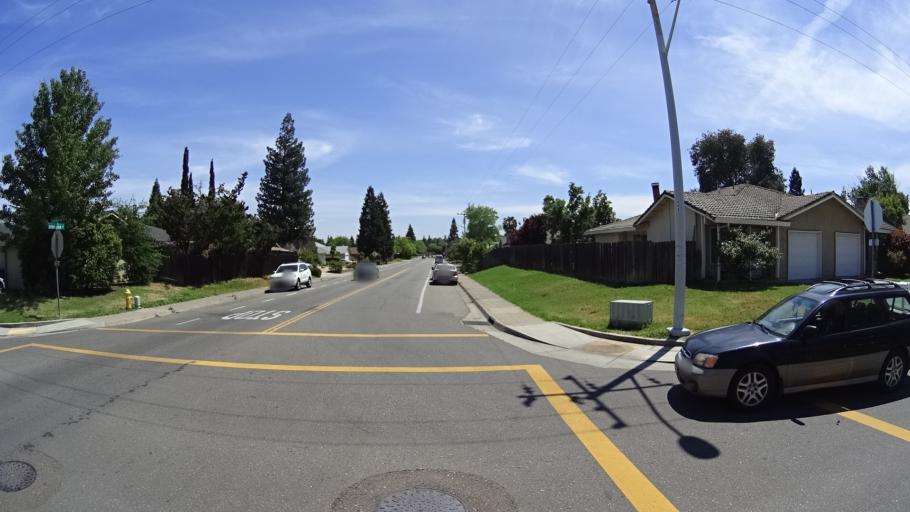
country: US
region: California
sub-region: Placer County
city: Rocklin
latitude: 38.7809
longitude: -121.2597
